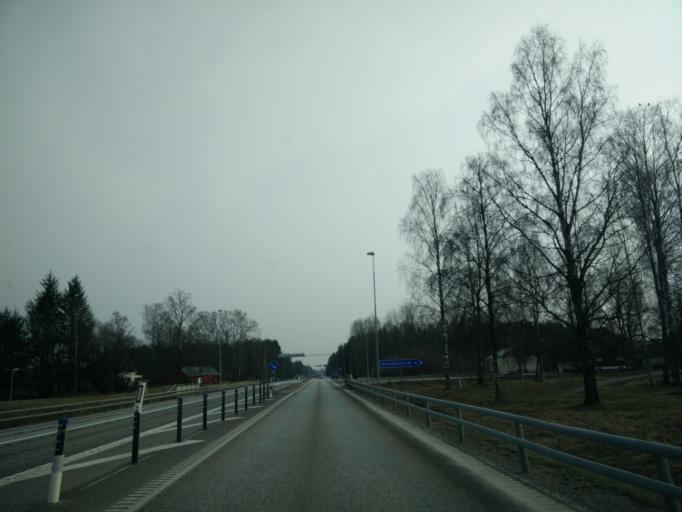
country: SE
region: Vaermland
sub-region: Forshaga Kommun
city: Forshaga
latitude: 59.4589
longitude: 13.4166
